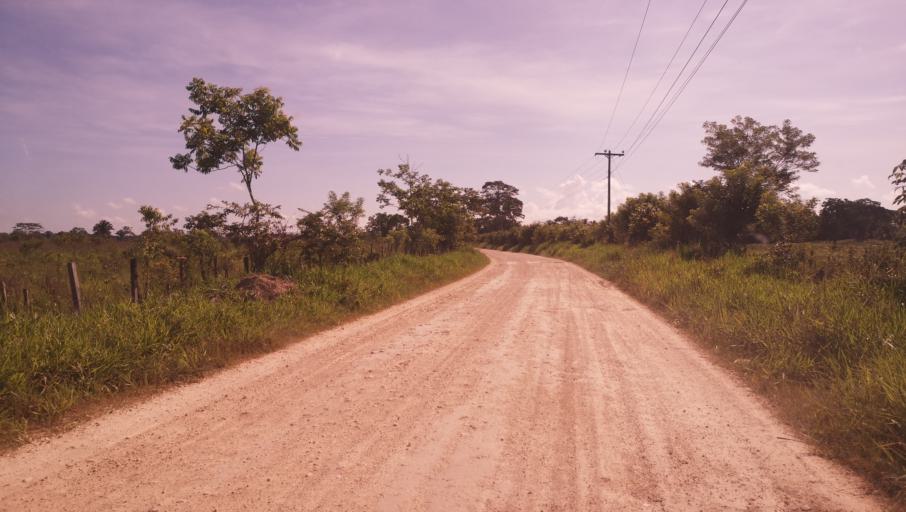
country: GT
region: Peten
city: Dolores
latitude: 16.7153
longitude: -89.3646
